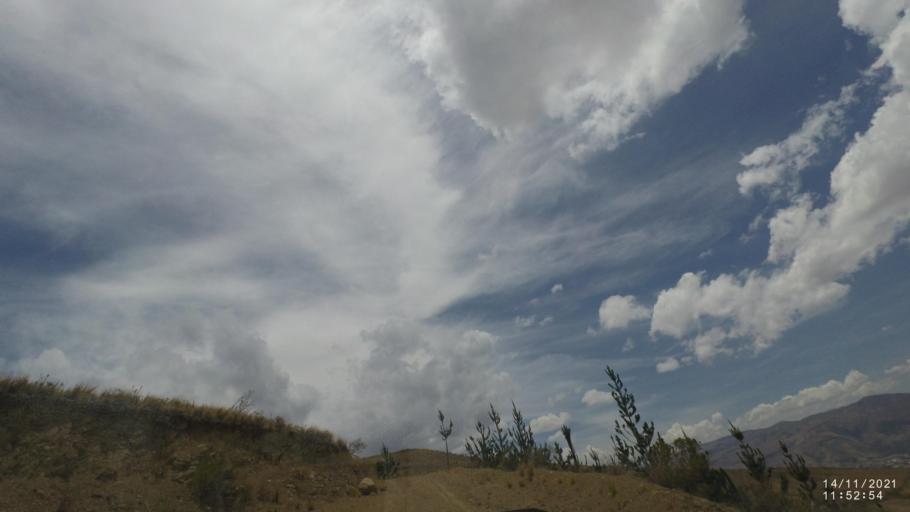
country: BO
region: Cochabamba
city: Colomi
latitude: -17.3638
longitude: -65.9823
